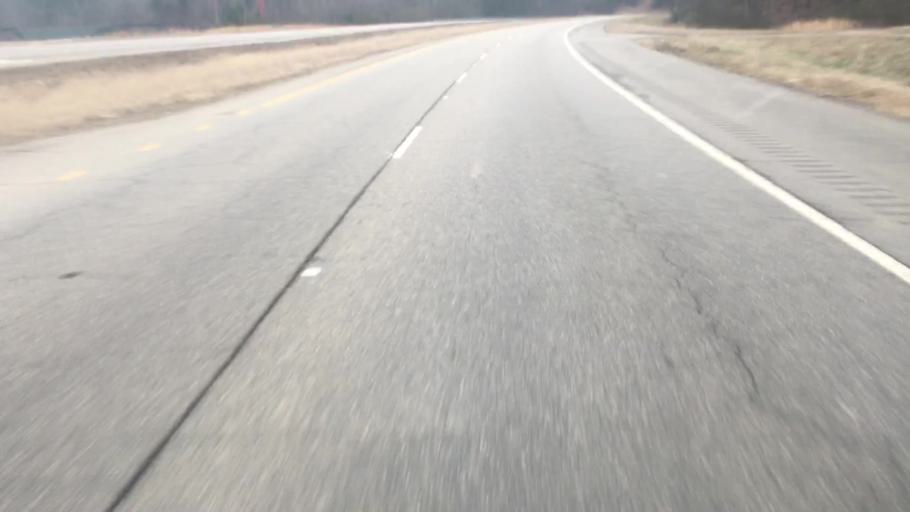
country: US
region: Alabama
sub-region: Walker County
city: Sumiton
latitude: 33.7739
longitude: -87.0751
